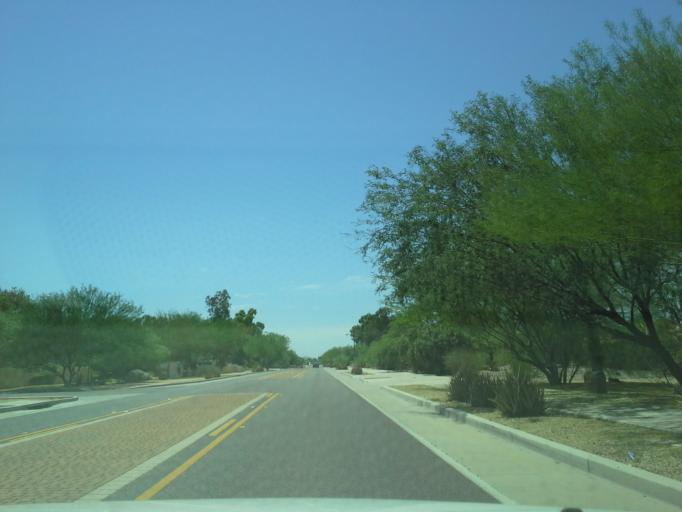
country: US
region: Arizona
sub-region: Maricopa County
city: Scottsdale
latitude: 33.5971
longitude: -111.8675
